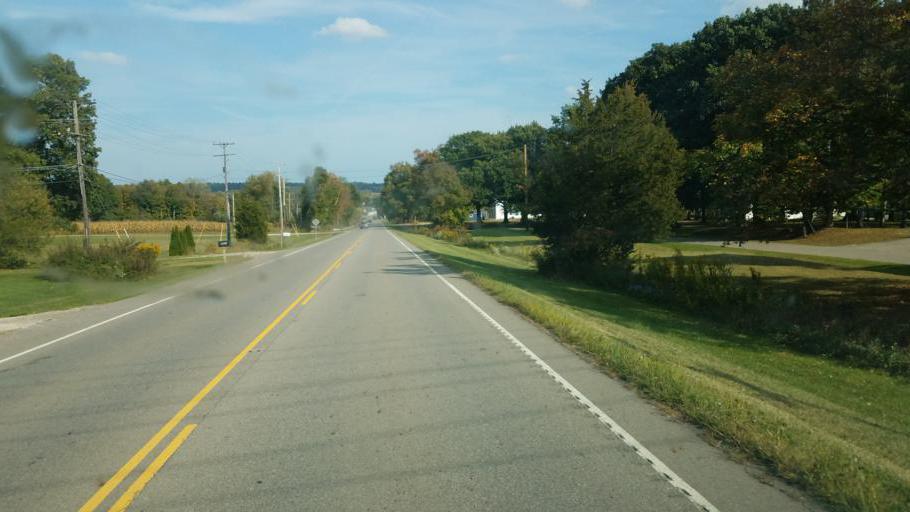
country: US
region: Ohio
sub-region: Licking County
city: Utica
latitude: 40.2309
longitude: -82.4634
